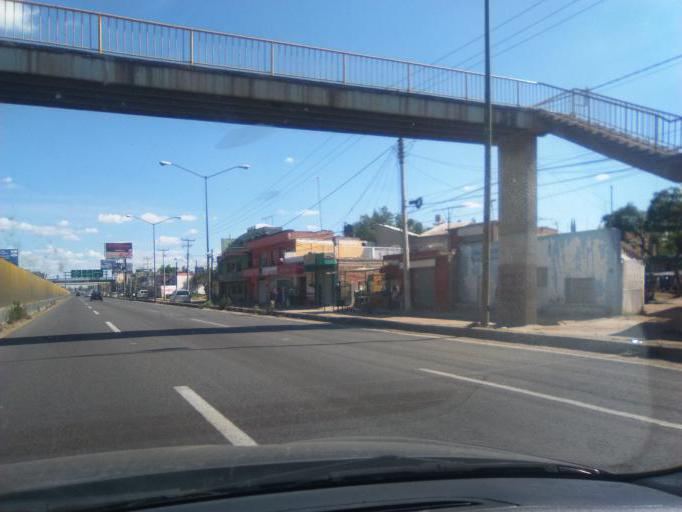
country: MX
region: Guanajuato
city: Colonia Nuevo Mexico
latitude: 20.9844
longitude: -101.4847
